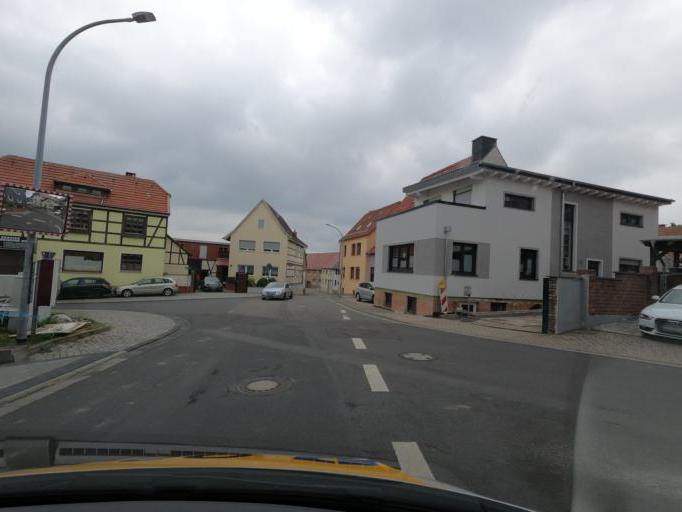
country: DE
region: Thuringia
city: Silberhausen
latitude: 51.3095
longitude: 10.3394
